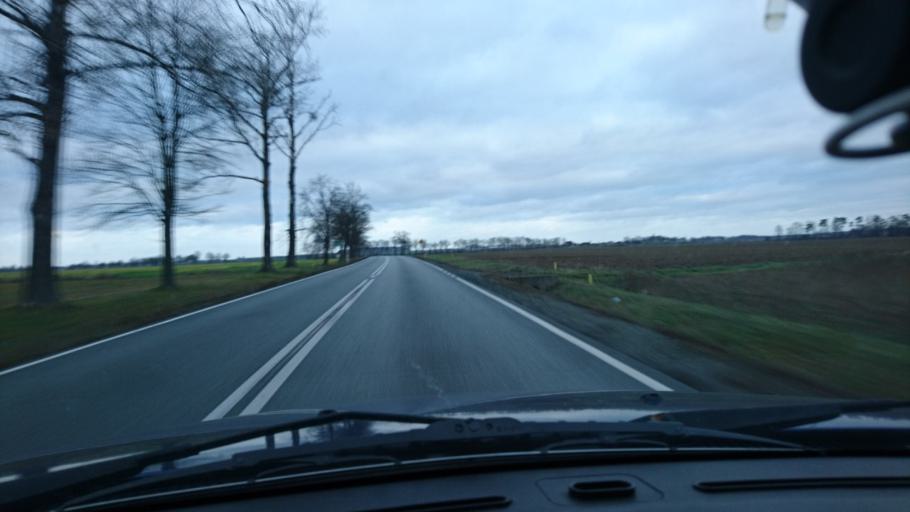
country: PL
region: Opole Voivodeship
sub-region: Powiat kluczborski
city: Byczyna
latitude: 51.0658
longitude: 18.2021
